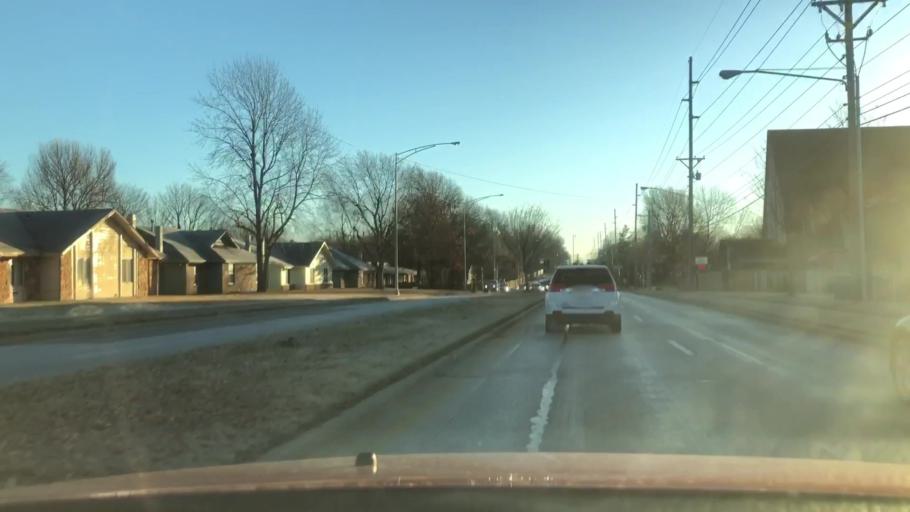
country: US
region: Missouri
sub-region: Greene County
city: Springfield
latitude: 37.1591
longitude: -93.2583
